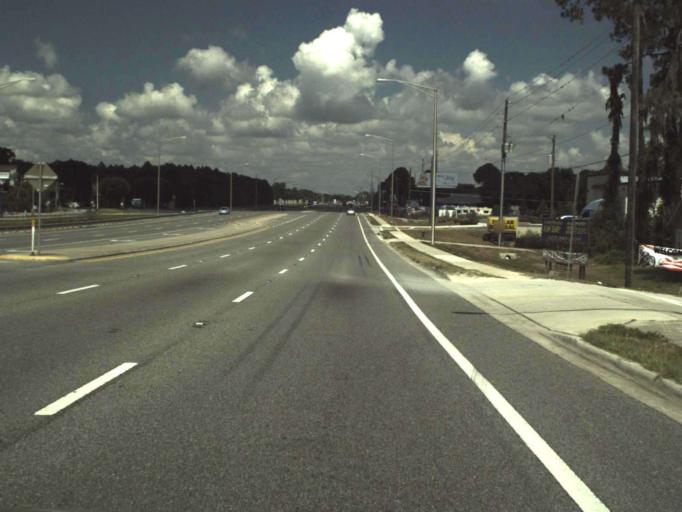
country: US
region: Florida
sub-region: Lake County
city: Tavares
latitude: 28.8160
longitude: -81.7621
